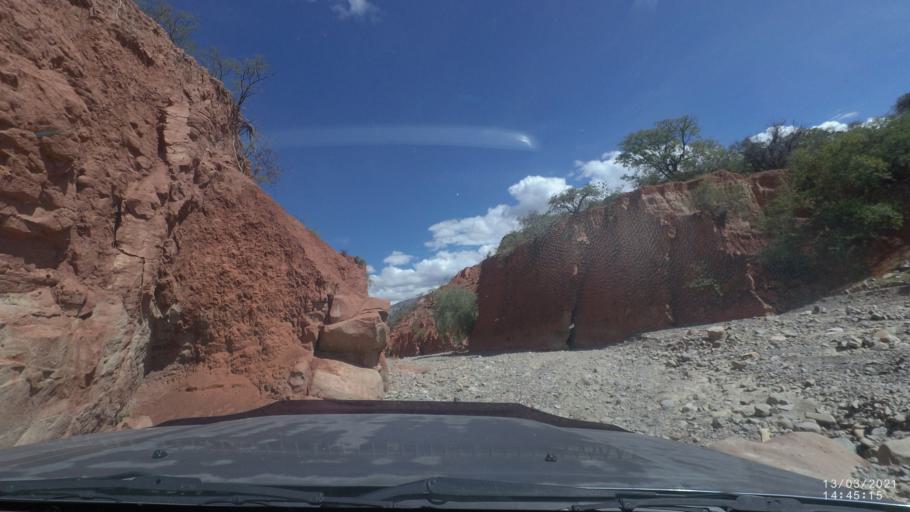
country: BO
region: Cochabamba
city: Cliza
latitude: -17.9426
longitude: -65.8600
